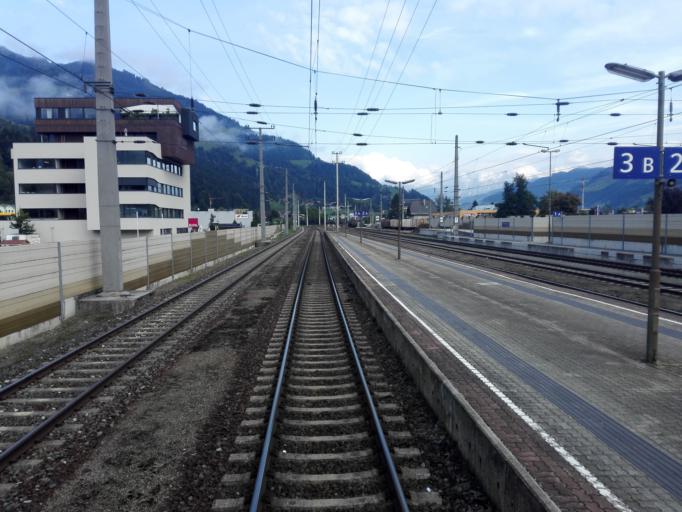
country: AT
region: Salzburg
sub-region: Politischer Bezirk Sankt Johann im Pongau
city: Sankt Johann im Pongau
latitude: 47.3491
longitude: 13.1949
